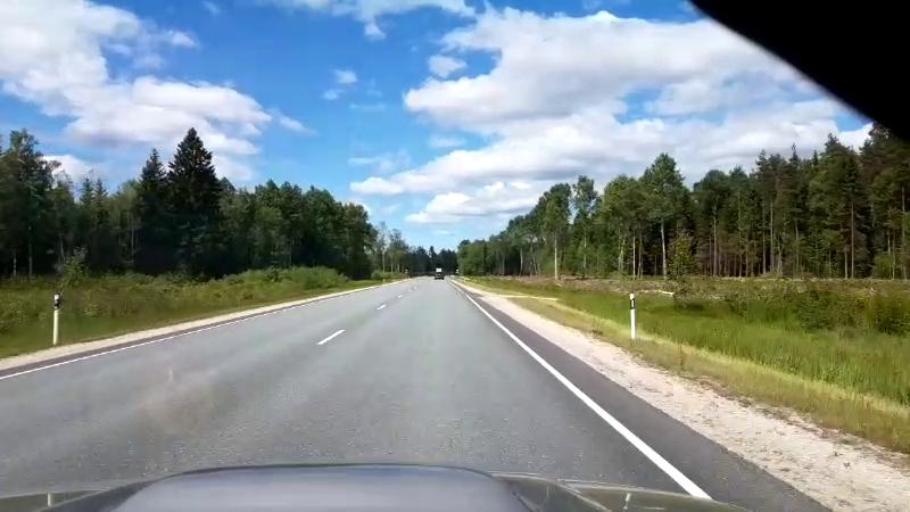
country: EE
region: Raplamaa
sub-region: Maerjamaa vald
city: Marjamaa
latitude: 59.0288
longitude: 24.4460
